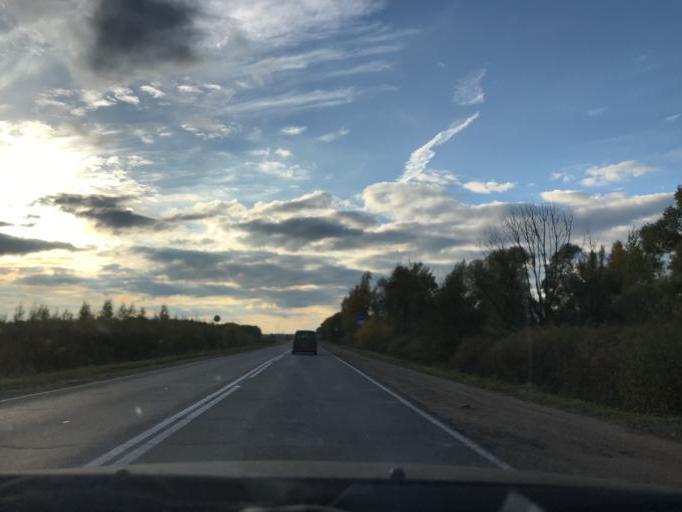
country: RU
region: Kaluga
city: Kurovskoye
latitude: 54.5292
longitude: 35.9630
